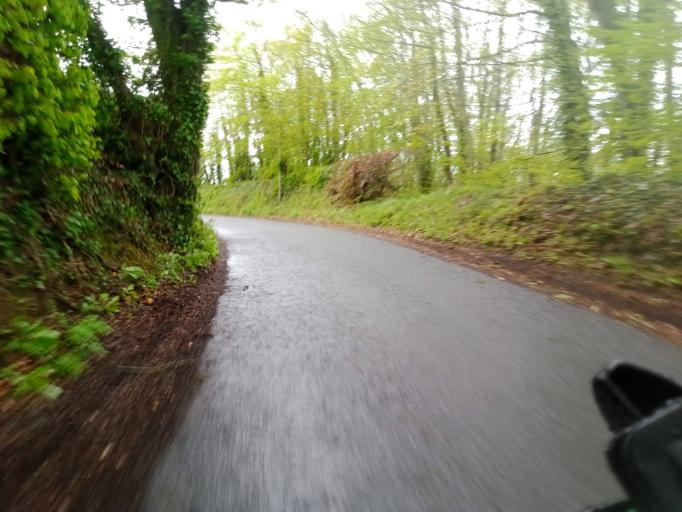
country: IE
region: Leinster
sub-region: Kilkenny
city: Kilkenny
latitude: 52.6832
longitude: -7.2681
